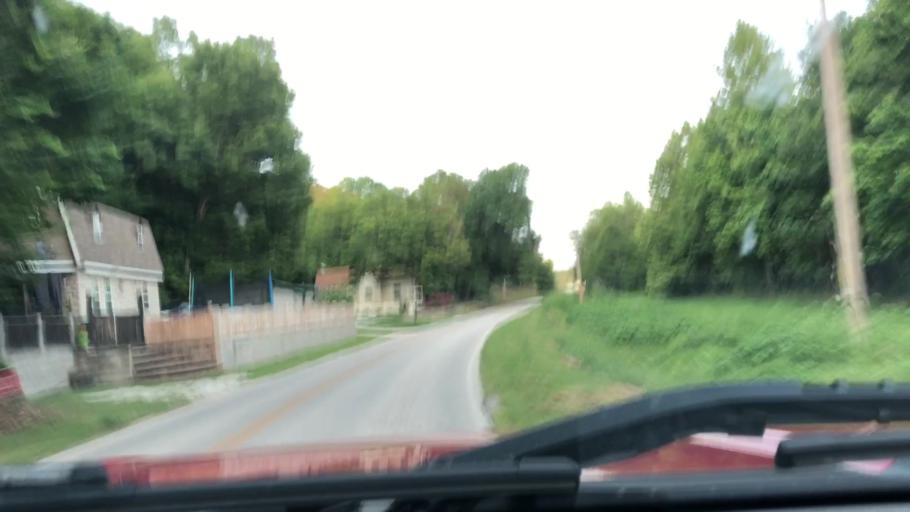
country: US
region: Missouri
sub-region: Jasper County
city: Duquesne
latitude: 37.0176
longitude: -94.4879
